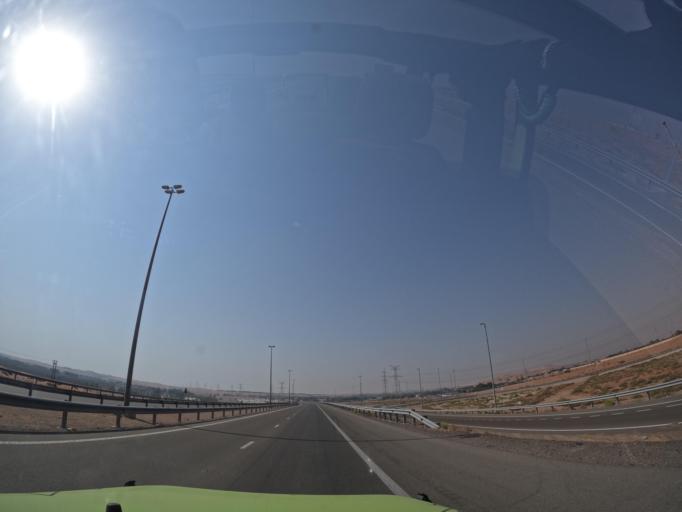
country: OM
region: Al Buraimi
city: Al Buraymi
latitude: 24.3719
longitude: 55.7284
